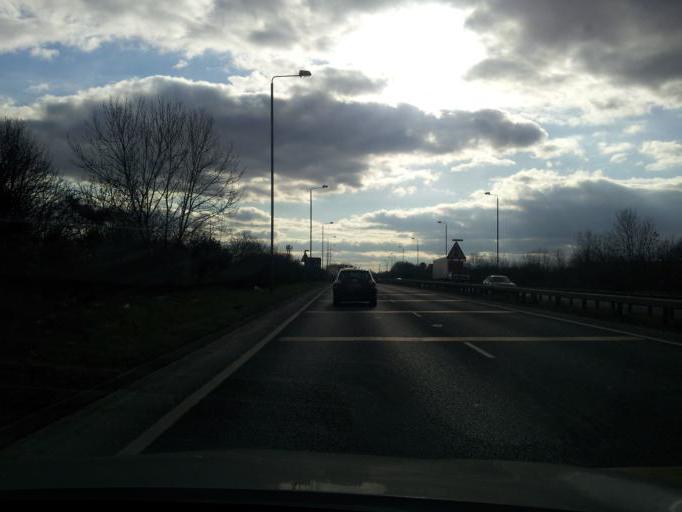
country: GB
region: England
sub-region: Derbyshire
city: Pinxton
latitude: 53.1058
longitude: -1.3187
